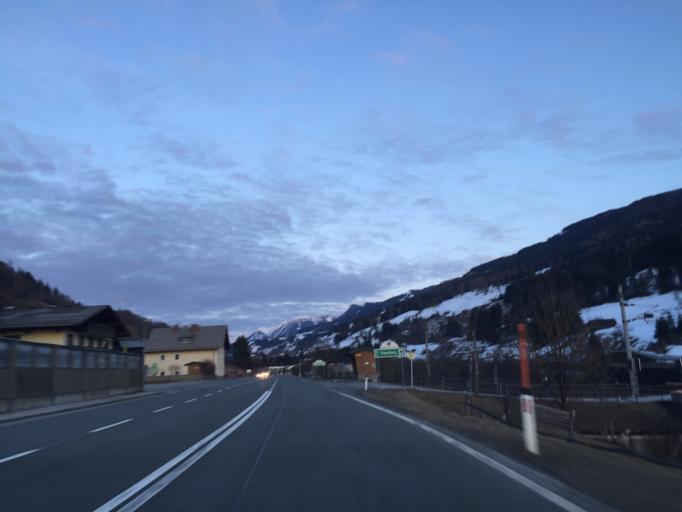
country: AT
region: Salzburg
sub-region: Politischer Bezirk Zell am See
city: Taxenbach
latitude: 47.2887
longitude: 12.9129
